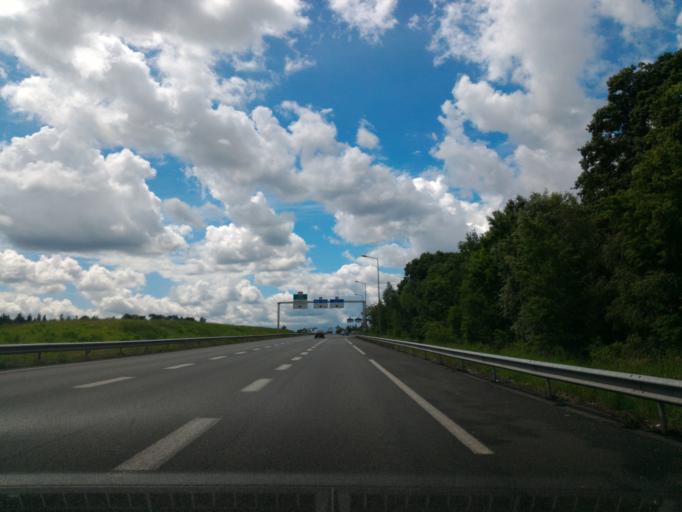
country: FR
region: Ile-de-France
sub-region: Departement de Seine-et-Marne
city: Lognes
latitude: 48.8339
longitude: 2.6217
